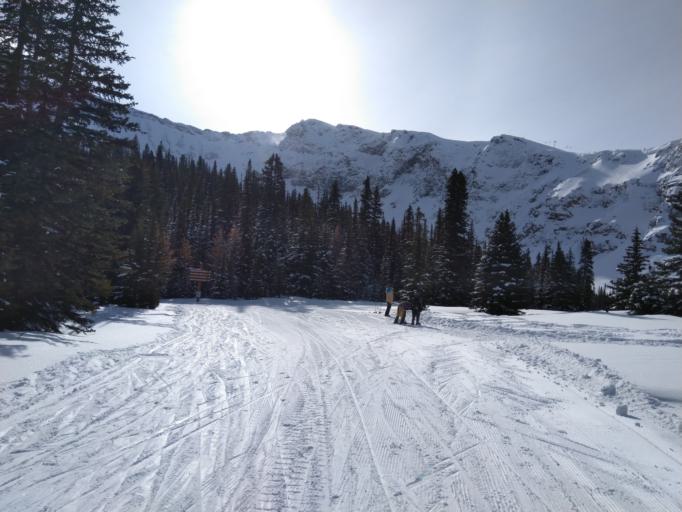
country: CA
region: Alberta
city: Banff
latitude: 51.0857
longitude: -115.7693
